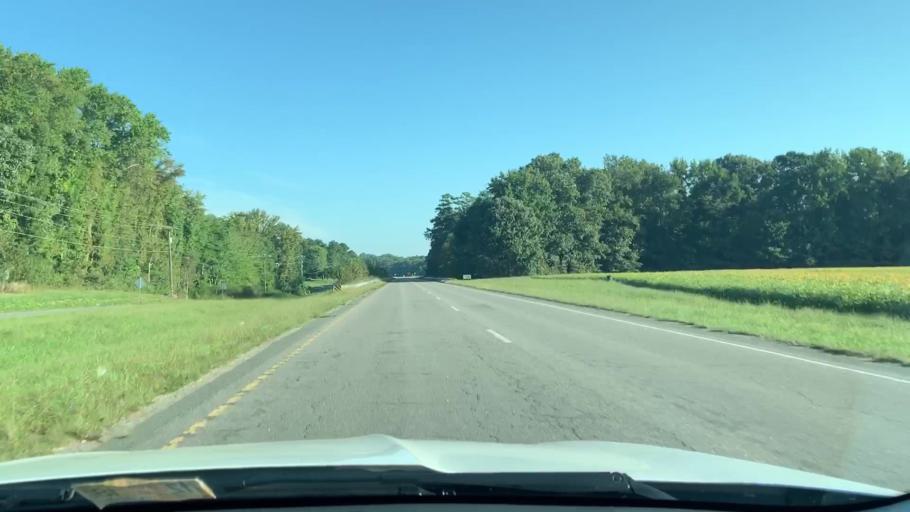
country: US
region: Virginia
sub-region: Lancaster County
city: Kilmarnock
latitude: 37.6887
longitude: -76.3761
